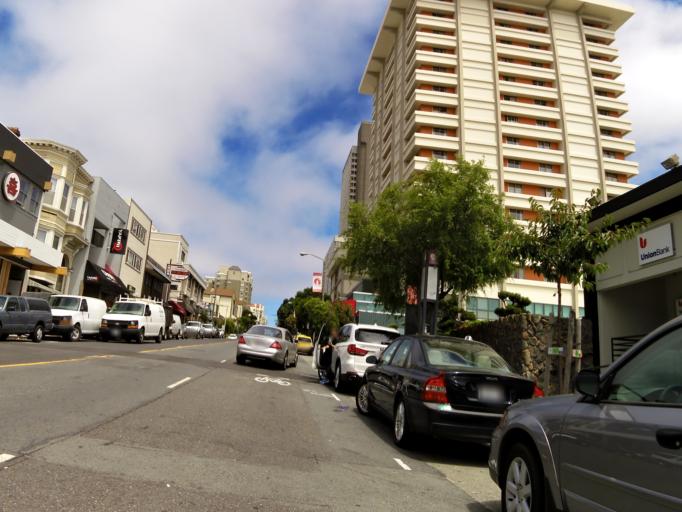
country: US
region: California
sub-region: San Francisco County
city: San Francisco
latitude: 37.7856
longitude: -122.4294
